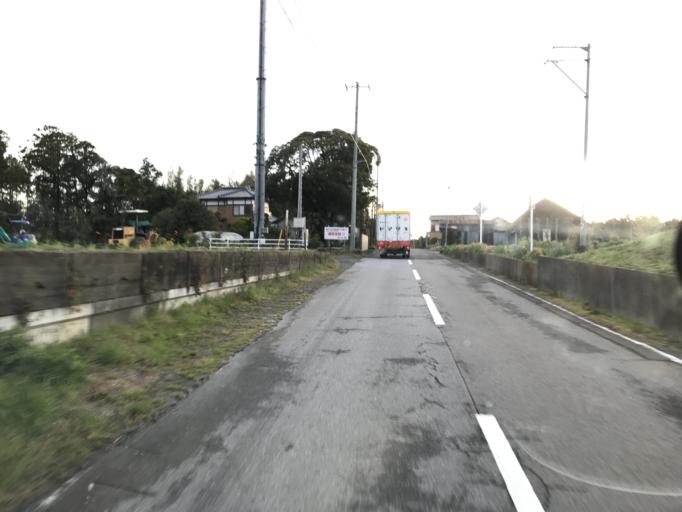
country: JP
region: Chiba
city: Yokaichiba
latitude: 35.7492
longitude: 140.5393
